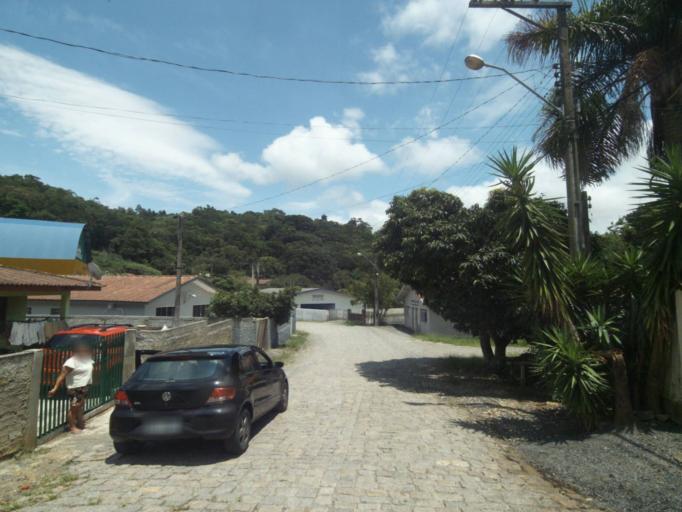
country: BR
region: Parana
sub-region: Campina Grande Do Sul
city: Campina Grande do Sul
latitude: -25.1112
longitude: -48.8359
